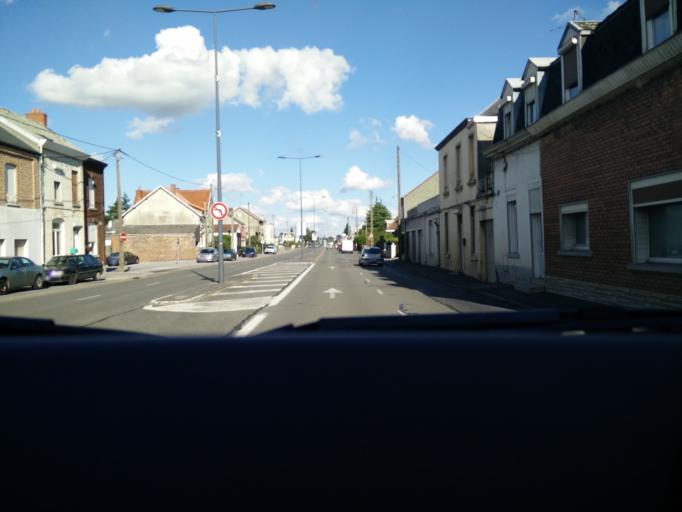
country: FR
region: Nord-Pas-de-Calais
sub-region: Departement du Nord
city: Maubeuge
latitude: 50.2822
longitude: 3.9652
